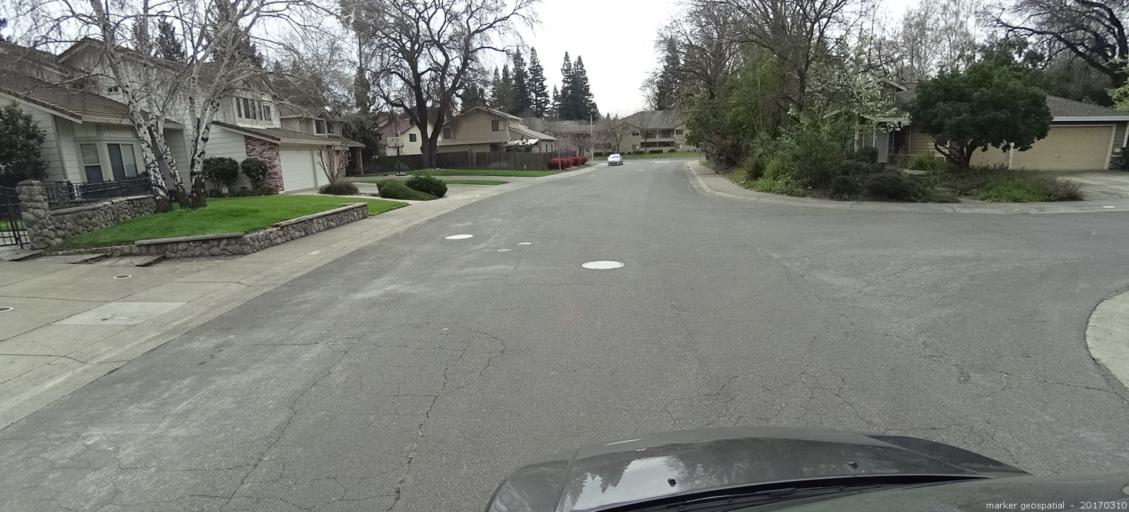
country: US
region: California
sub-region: Sacramento County
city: Parkway
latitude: 38.4846
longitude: -121.5191
